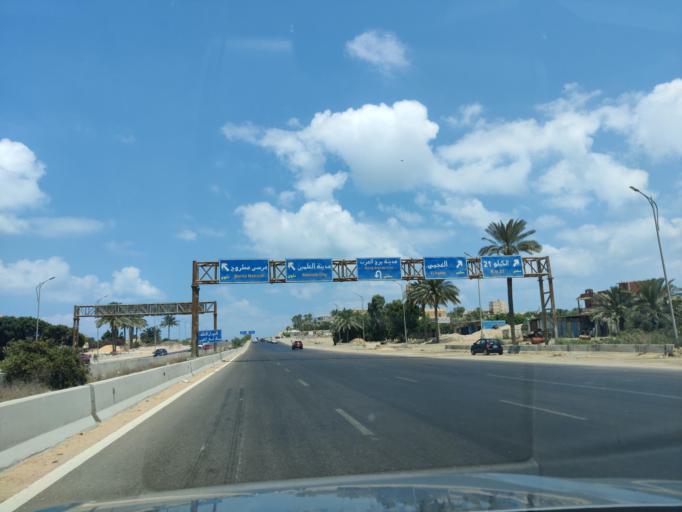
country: EG
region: Alexandria
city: Alexandria
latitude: 31.0081
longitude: 29.6381
